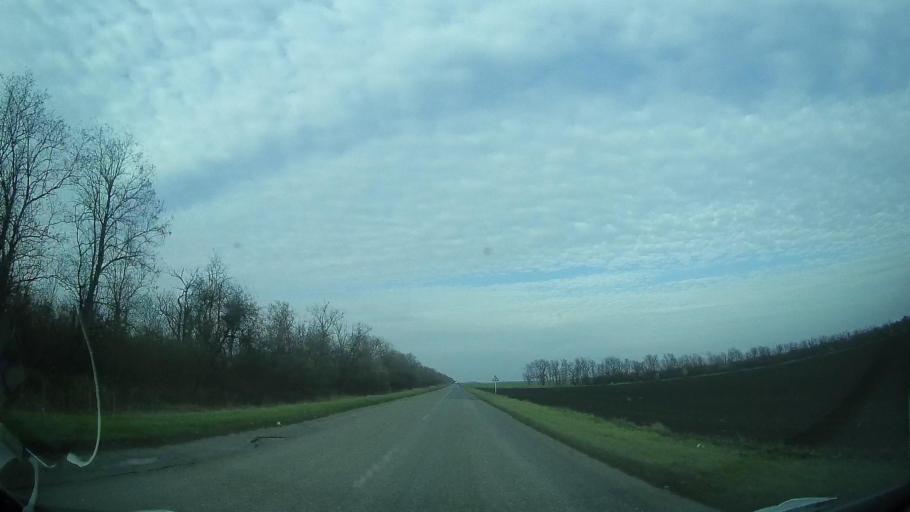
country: RU
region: Rostov
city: Zernograd
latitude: 46.9380
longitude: 40.3665
